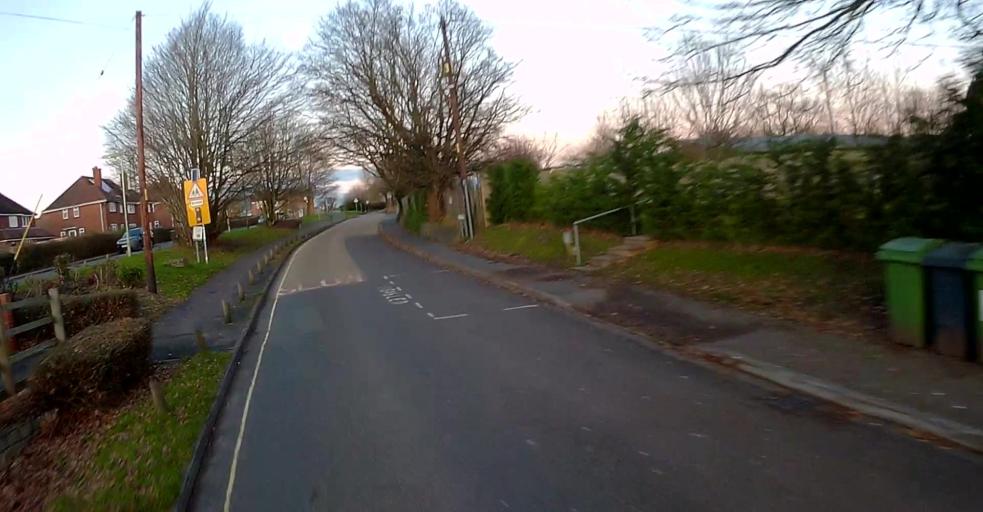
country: GB
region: England
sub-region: West Berkshire
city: Stratfield Mortimer
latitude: 51.3325
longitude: -1.0593
